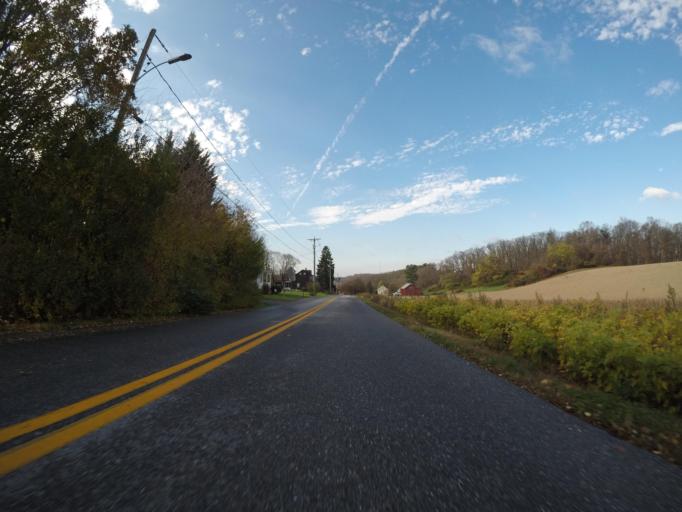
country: US
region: Maryland
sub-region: Carroll County
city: Hampstead
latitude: 39.5807
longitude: -76.8048
